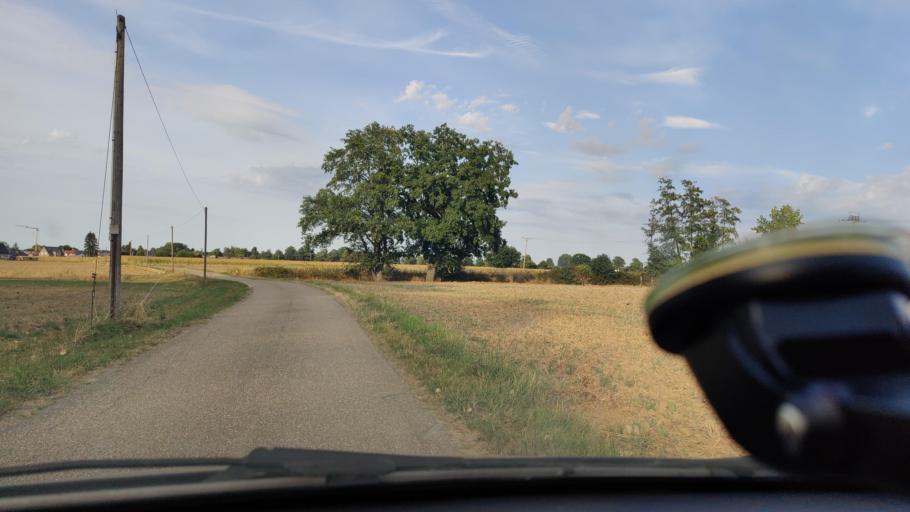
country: DE
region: North Rhine-Westphalia
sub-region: Regierungsbezirk Dusseldorf
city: Sonsbeck
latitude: 51.5627
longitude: 6.3644
